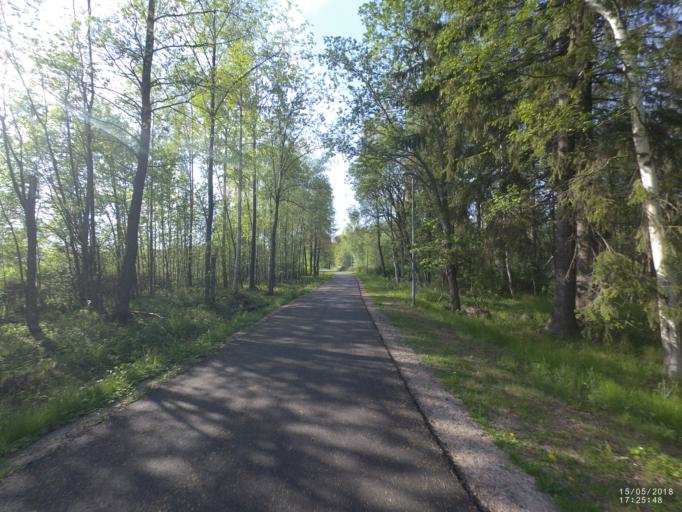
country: SE
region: Soedermanland
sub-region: Nykopings Kommun
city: Nykoping
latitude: 58.7198
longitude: 17.0288
